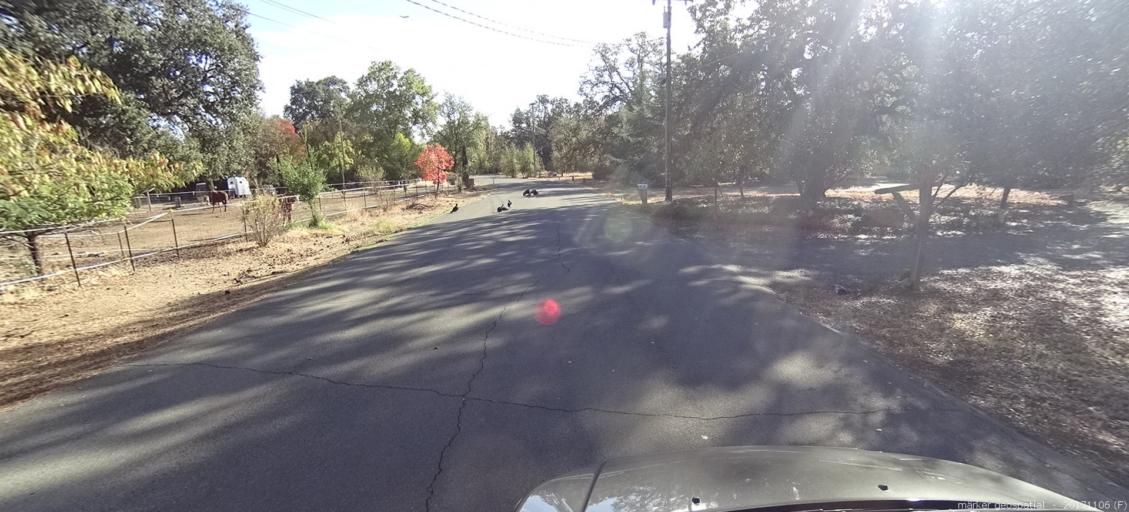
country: US
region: California
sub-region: Shasta County
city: Palo Cedro
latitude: 40.5434
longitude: -122.2472
